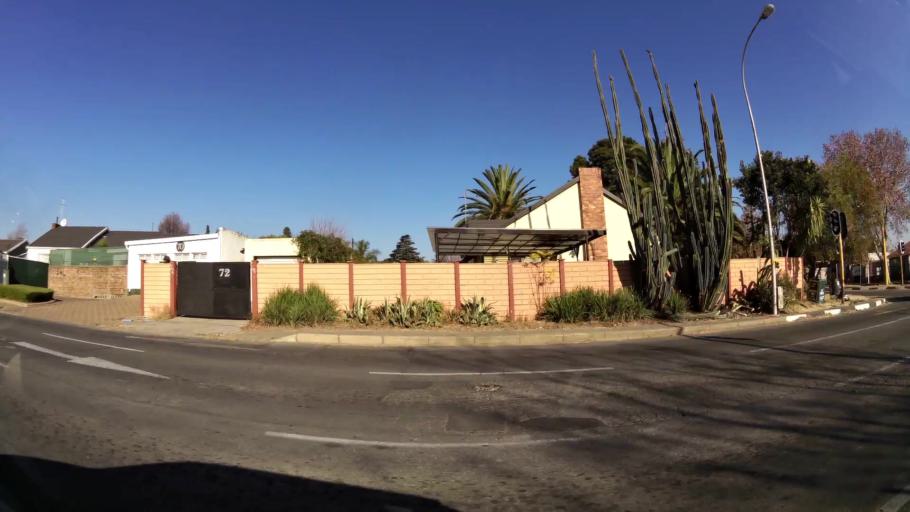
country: ZA
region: Gauteng
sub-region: City of Johannesburg Metropolitan Municipality
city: Modderfontein
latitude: -26.1387
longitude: 28.1586
